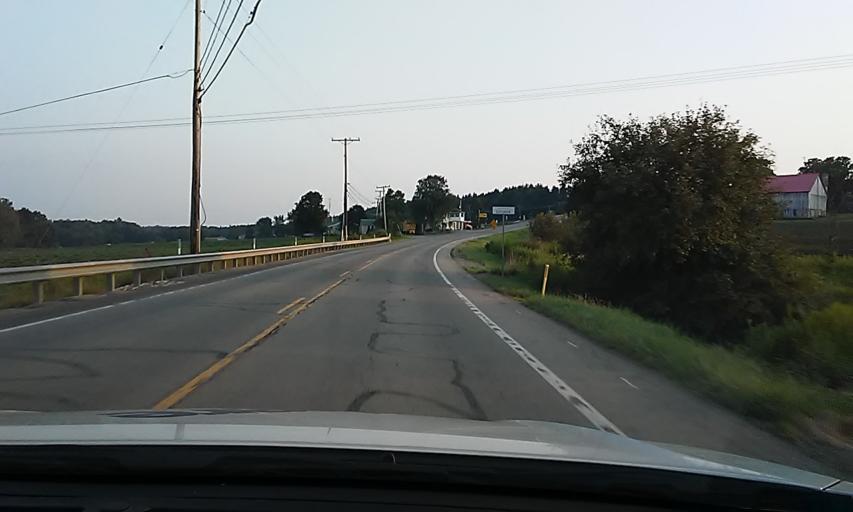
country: US
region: Pennsylvania
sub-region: Clarion County
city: Marianne
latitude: 41.3170
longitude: -79.3613
